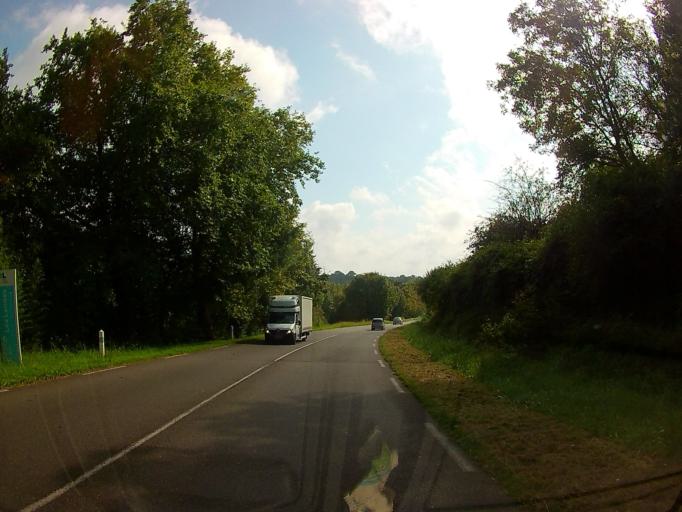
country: FR
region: Aquitaine
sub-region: Departement des Pyrenees-Atlantiques
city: Boucau
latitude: 43.5197
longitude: -1.4642
